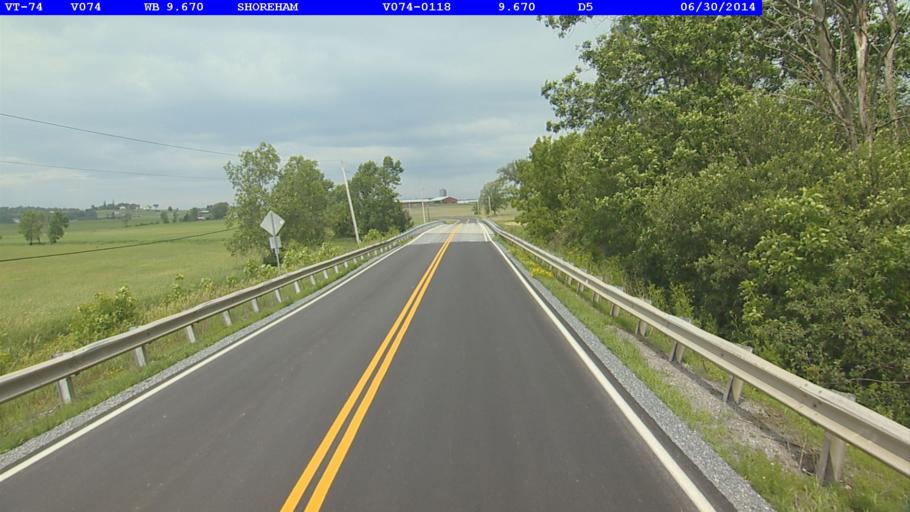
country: US
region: Vermont
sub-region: Addison County
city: Middlebury (village)
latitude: 43.9422
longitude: -73.2618
